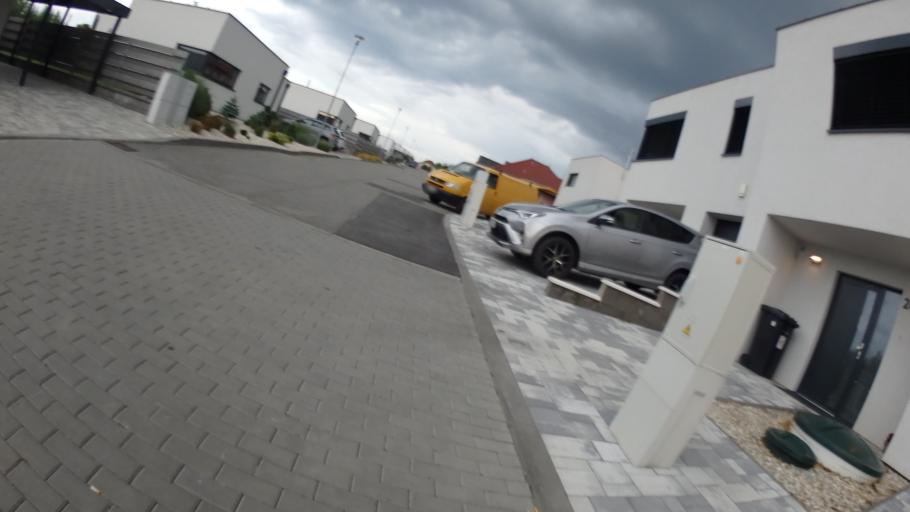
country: CZ
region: South Moravian
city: Ostopovice
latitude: 49.1395
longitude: 16.5501
